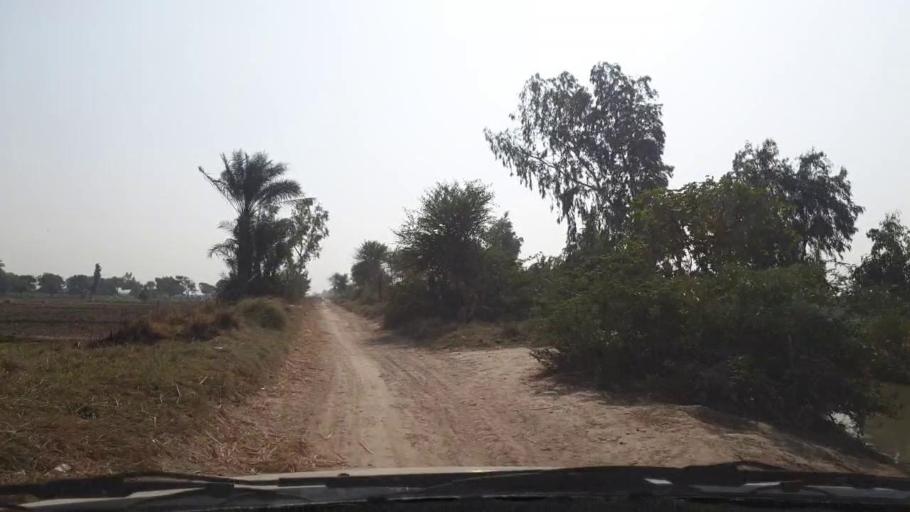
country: PK
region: Sindh
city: Tando Muhammad Khan
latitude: 25.0768
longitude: 68.3623
